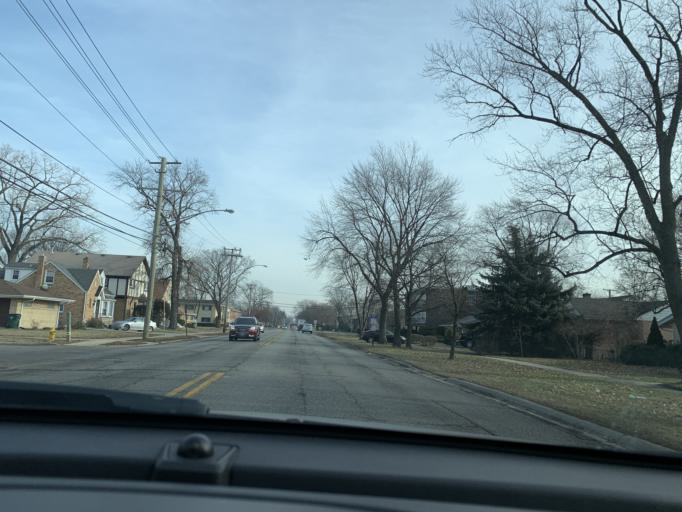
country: US
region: Illinois
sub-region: Cook County
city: Park Ridge
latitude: 42.0105
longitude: -87.8520
